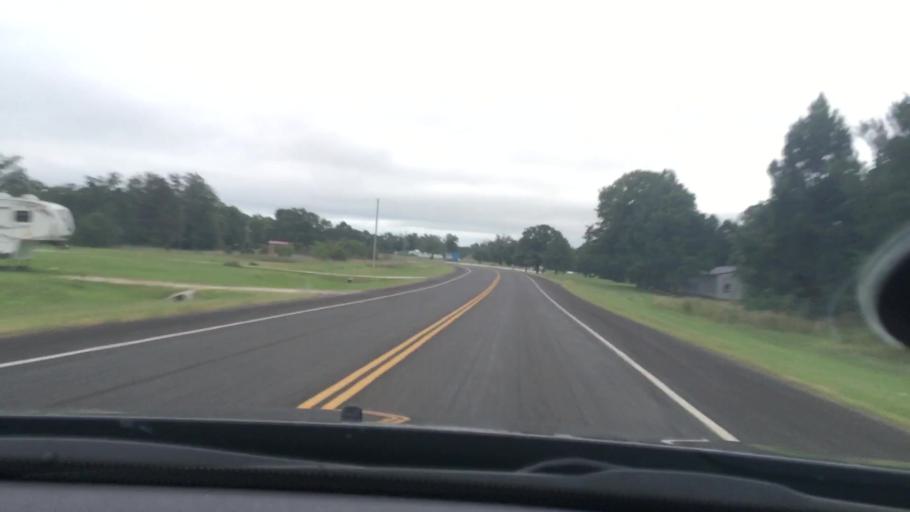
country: US
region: Oklahoma
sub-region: Sequoyah County
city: Vian
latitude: 35.5583
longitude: -94.9798
